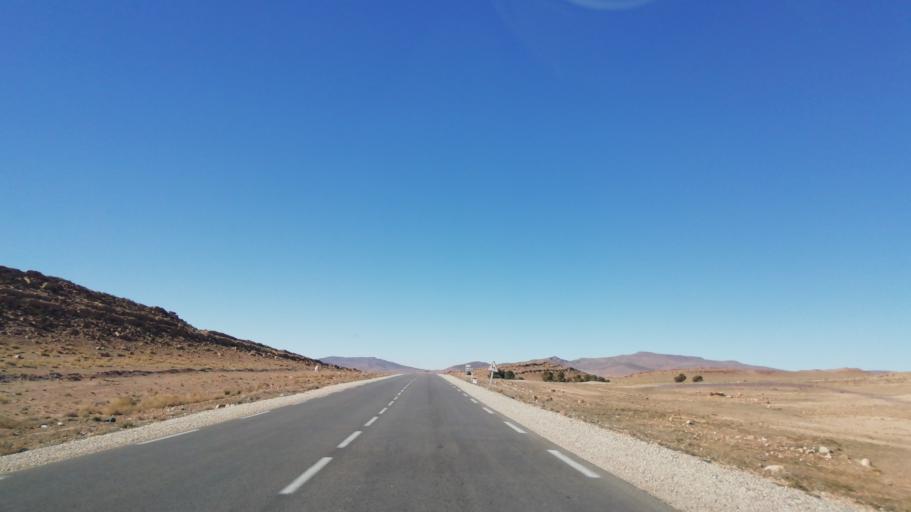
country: DZ
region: El Bayadh
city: El Bayadh
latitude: 33.6101
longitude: 1.2337
